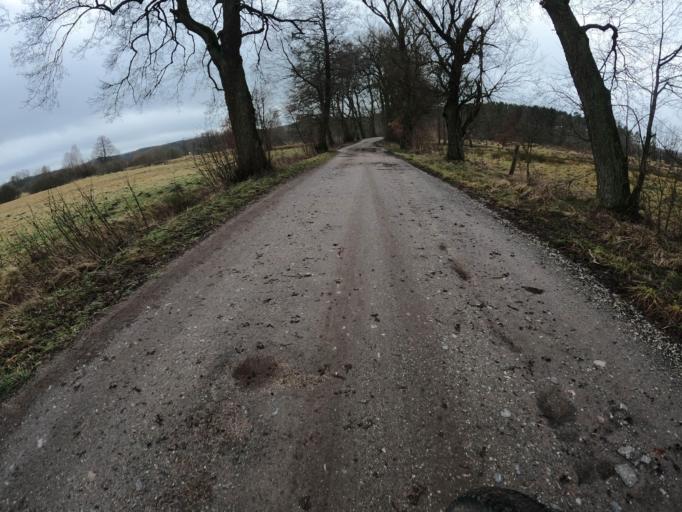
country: PL
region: West Pomeranian Voivodeship
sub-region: Powiat slawienski
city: Slawno
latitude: 54.2535
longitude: 16.6443
